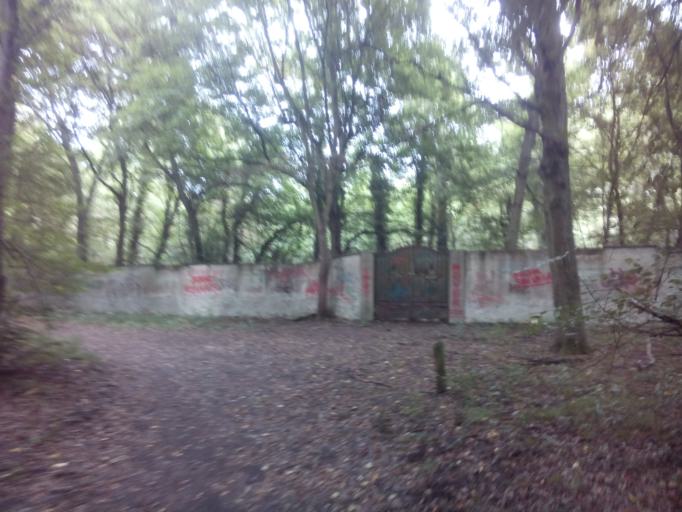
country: FR
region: Ile-de-France
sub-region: Departement du Val-d'Oise
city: Seugy
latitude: 49.1468
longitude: 2.3924
